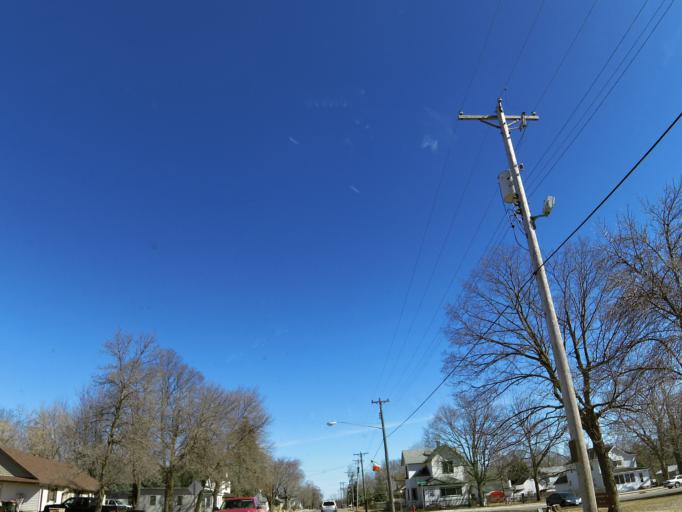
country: US
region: Minnesota
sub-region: Wright County
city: Maple Lake
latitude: 45.2296
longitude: -93.9997
